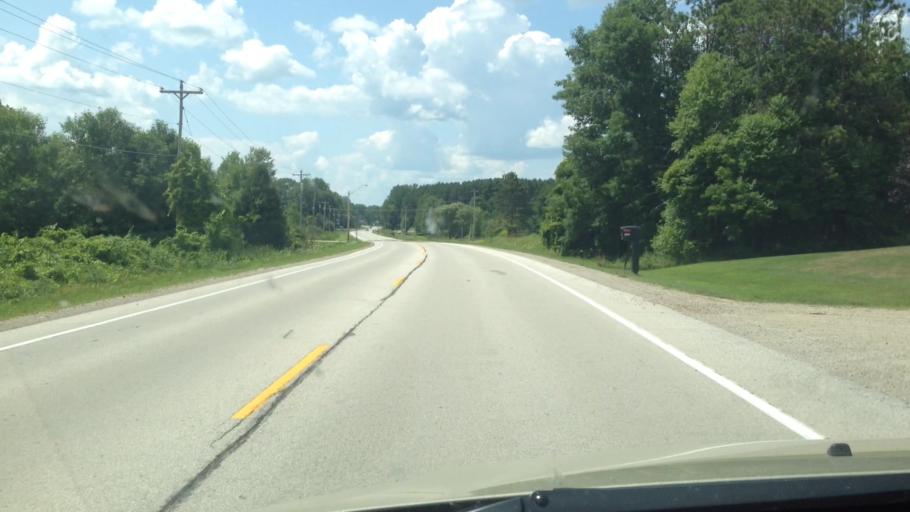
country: US
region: Wisconsin
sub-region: Brown County
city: Suamico
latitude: 44.6462
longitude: -88.0983
